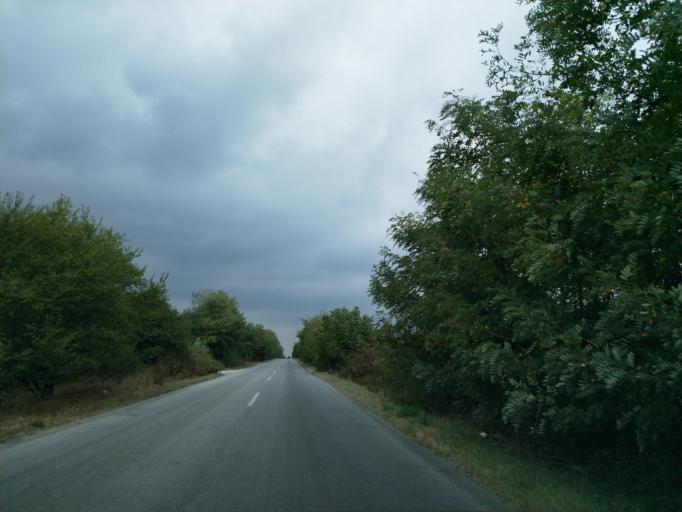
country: RS
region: Central Serbia
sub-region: Pomoravski Okrug
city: Jagodina
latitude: 43.9953
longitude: 21.2221
